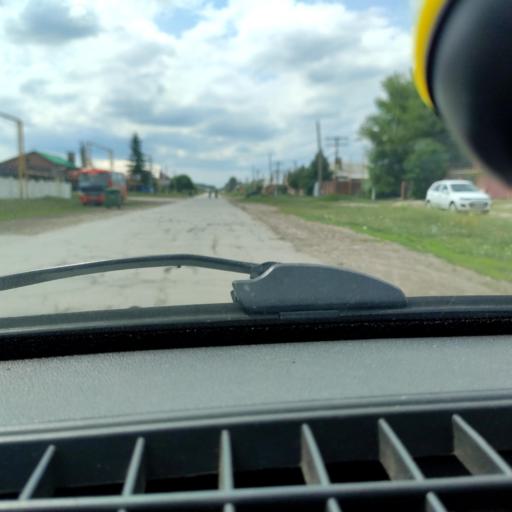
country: RU
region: Samara
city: Povolzhskiy
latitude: 53.6432
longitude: 49.6914
